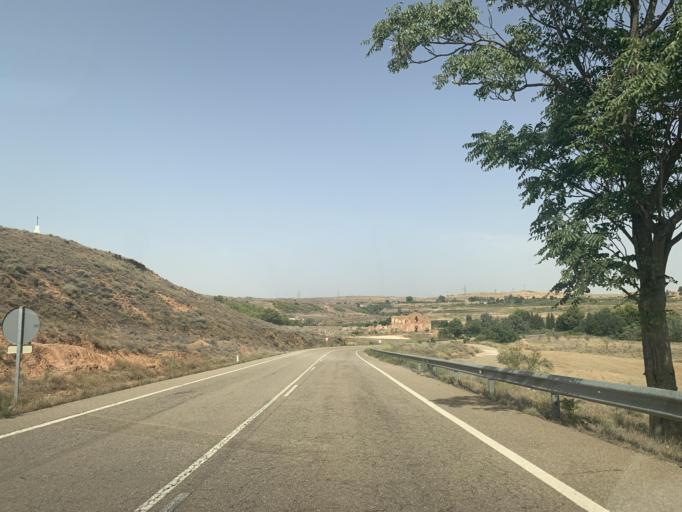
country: ES
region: Aragon
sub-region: Provincia de Zaragoza
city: Belchite
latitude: 41.2911
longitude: -0.7347
